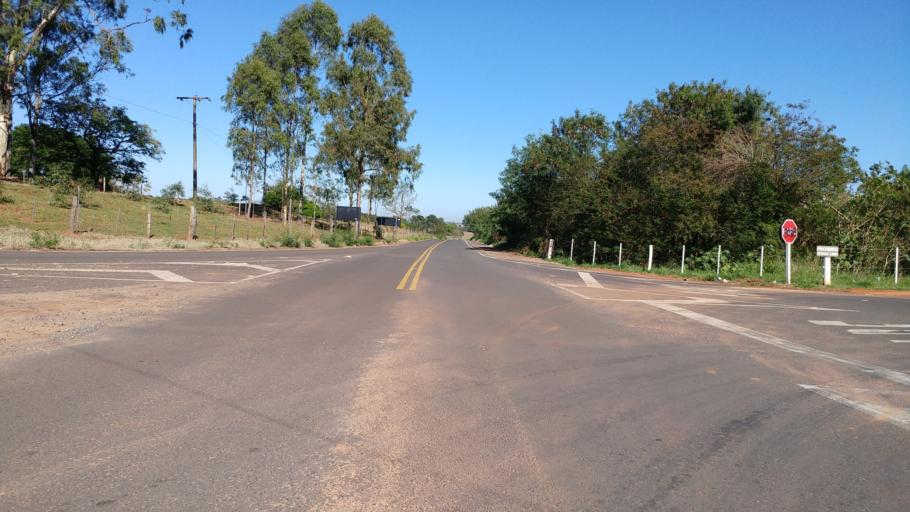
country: BR
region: Sao Paulo
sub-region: Paraguacu Paulista
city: Paraguacu Paulista
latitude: -22.4183
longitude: -50.5937
